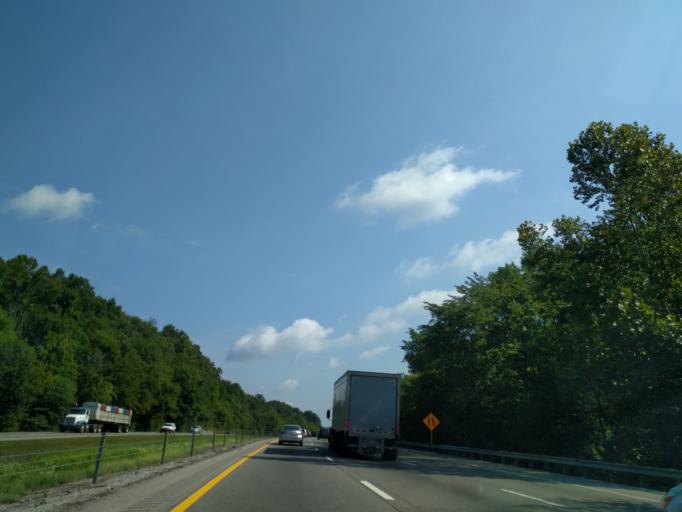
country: US
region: Tennessee
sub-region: Sumner County
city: Millersville
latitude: 36.3589
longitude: -86.7199
